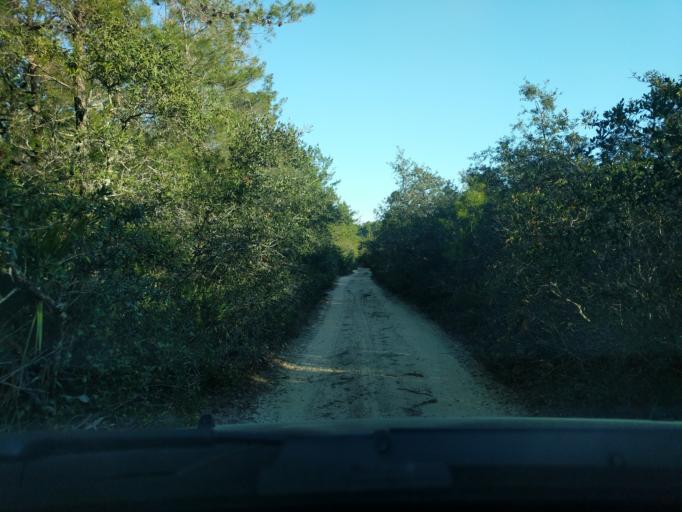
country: US
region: Florida
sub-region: Lake County
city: Astor
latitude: 29.2085
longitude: -81.7407
